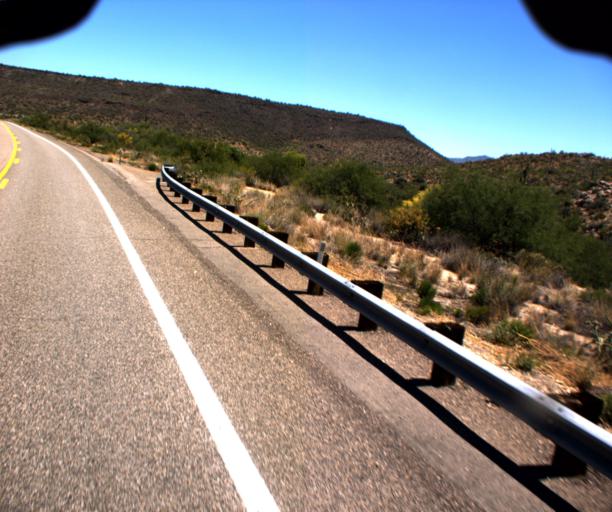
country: US
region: Arizona
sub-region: Yavapai County
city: Bagdad
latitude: 34.5163
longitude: -113.0865
